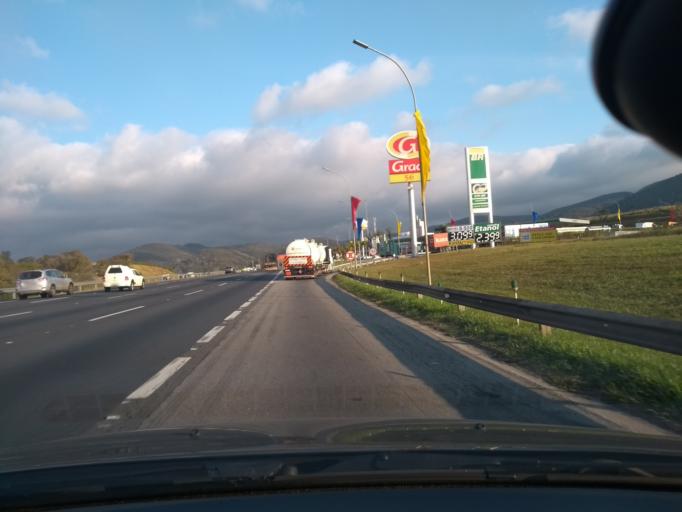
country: BR
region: Sao Paulo
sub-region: Jundiai
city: Jundiai
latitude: -23.2027
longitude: -46.9276
